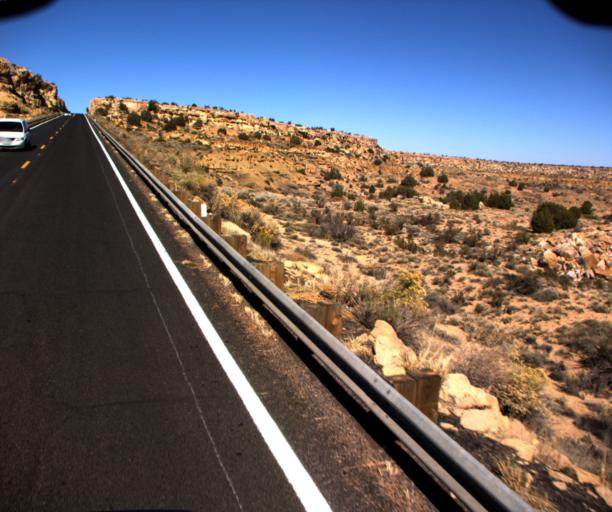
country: US
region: Arizona
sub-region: Navajo County
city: First Mesa
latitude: 35.8982
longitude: -110.6644
